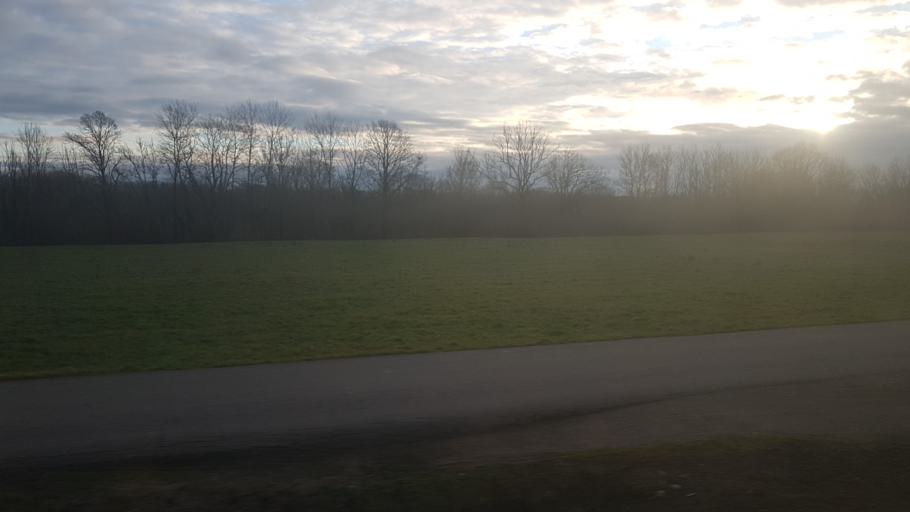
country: FR
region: Lorraine
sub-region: Departement des Vosges
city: Igney
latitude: 48.2815
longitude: 6.3983
